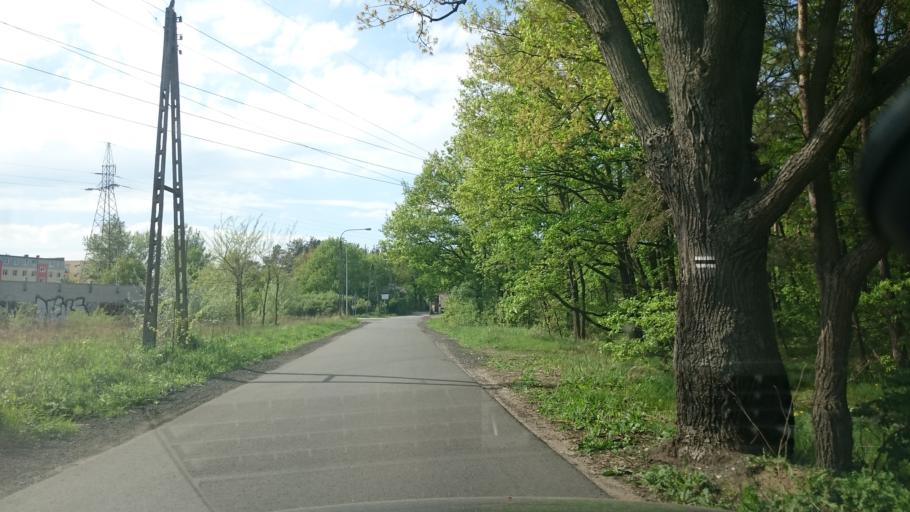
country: PL
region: Kujawsko-Pomorskie
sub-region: Grudziadz
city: Grudziadz
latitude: 53.4570
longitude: 18.7209
